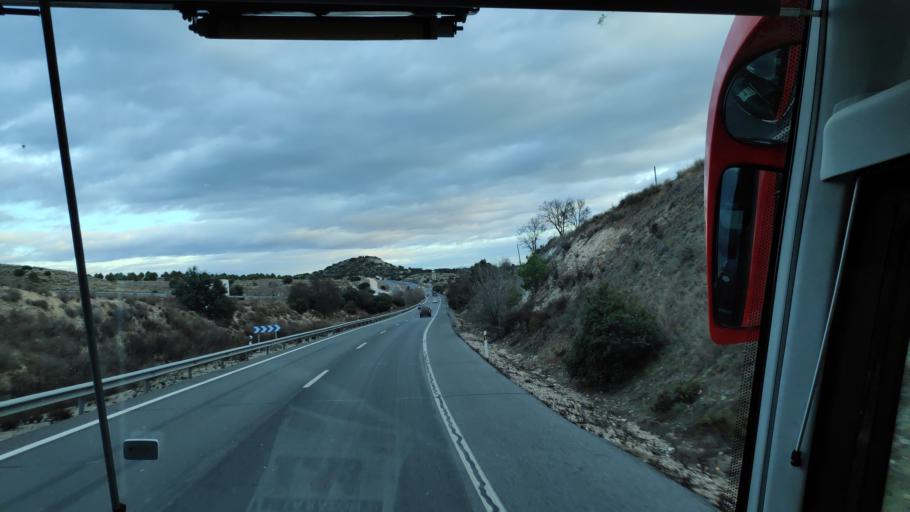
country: ES
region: Madrid
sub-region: Provincia de Madrid
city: Villarejo de Salvanes
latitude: 40.1476
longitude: -3.2190
